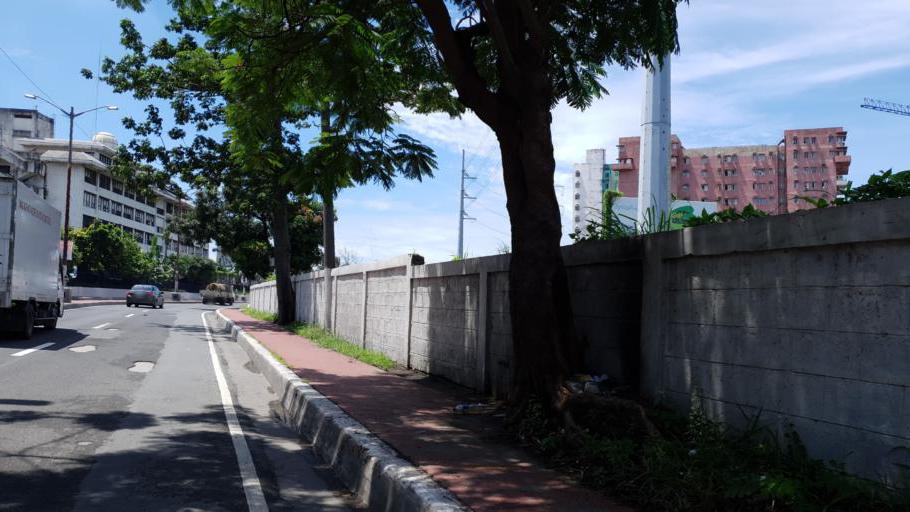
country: PH
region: Metro Manila
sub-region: San Juan
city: San Juan
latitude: 14.5970
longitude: 121.0137
